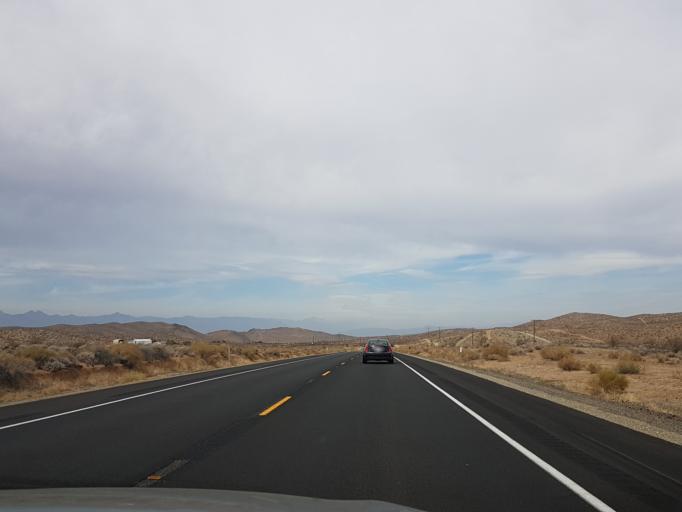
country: US
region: California
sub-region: Kern County
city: Ridgecrest
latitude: 35.5160
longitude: -117.6713
